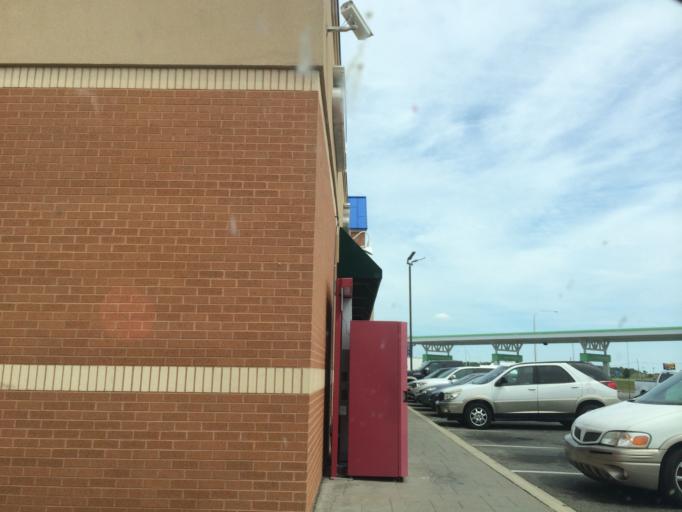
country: US
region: Delaware
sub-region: Sussex County
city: Bridgeville
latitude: 38.7239
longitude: -75.5895
